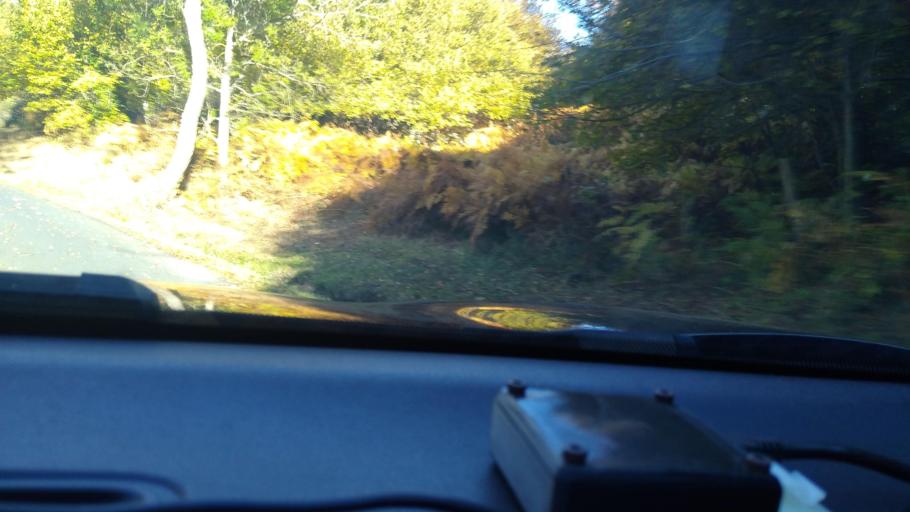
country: FR
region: Languedoc-Roussillon
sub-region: Departement de l'Aude
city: Quillan
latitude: 42.7345
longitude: 2.1355
